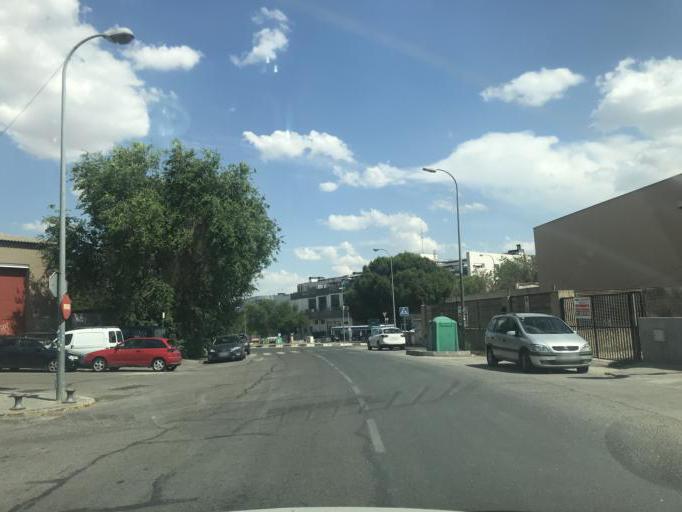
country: ES
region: Madrid
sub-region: Provincia de Madrid
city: Alcobendas
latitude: 40.5358
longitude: -3.6483
